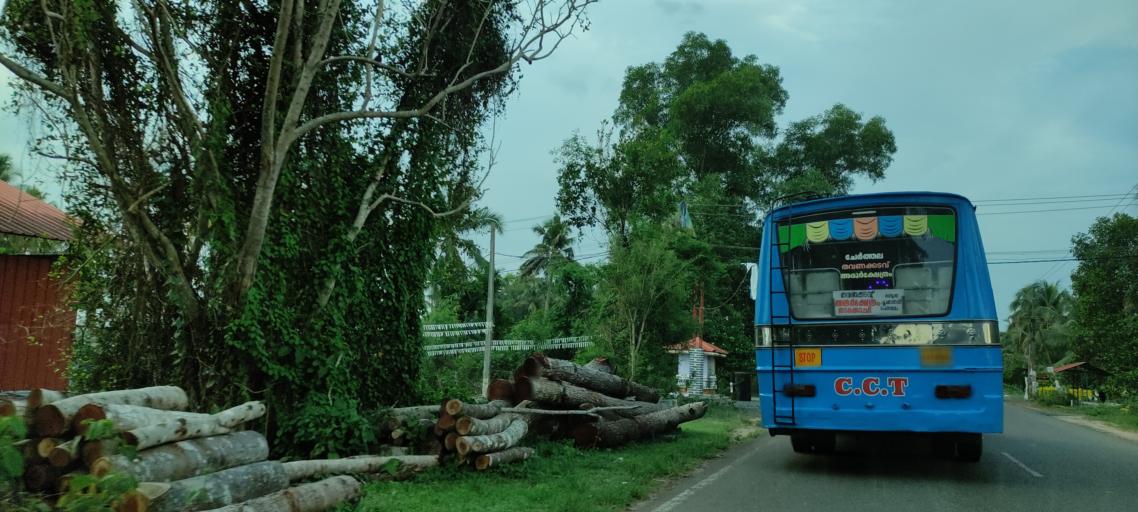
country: IN
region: Kerala
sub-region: Alappuzha
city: Kutiatodu
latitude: 9.7800
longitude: 76.3607
